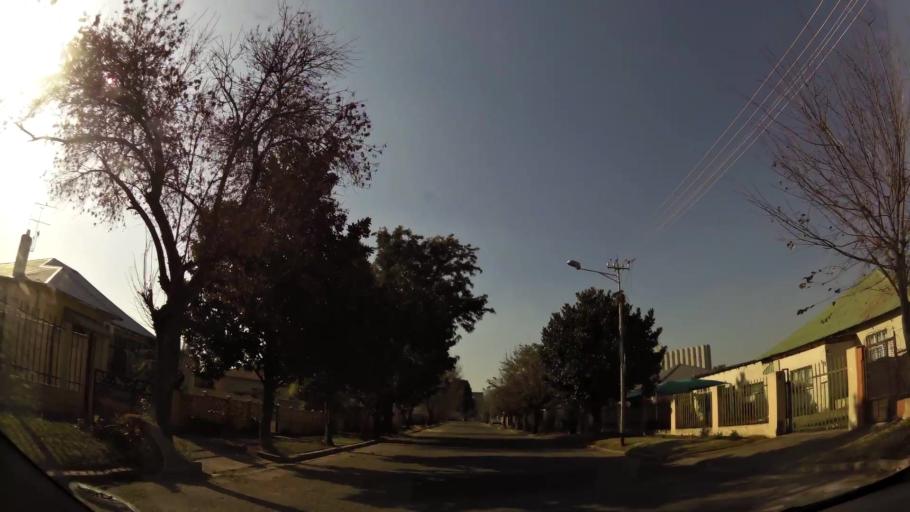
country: ZA
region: Gauteng
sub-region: West Rand District Municipality
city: Randfontein
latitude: -26.1688
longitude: 27.7082
